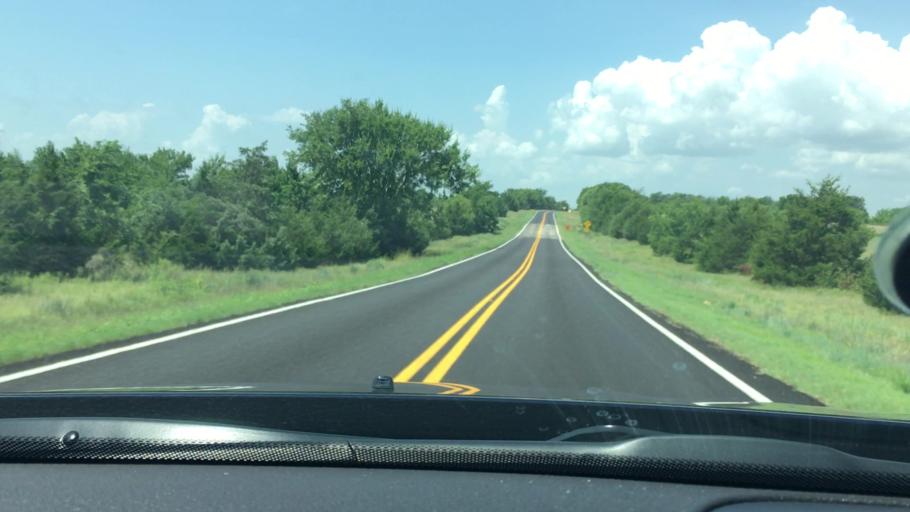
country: US
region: Oklahoma
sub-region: Marshall County
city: Kingston
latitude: 34.0883
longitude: -96.5957
